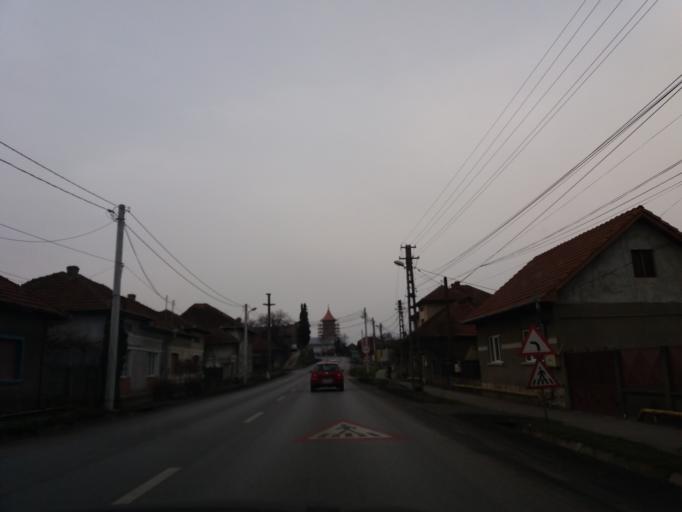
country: RO
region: Hunedoara
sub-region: Oras Simeria
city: Simeria
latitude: 45.8424
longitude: 23.0161
